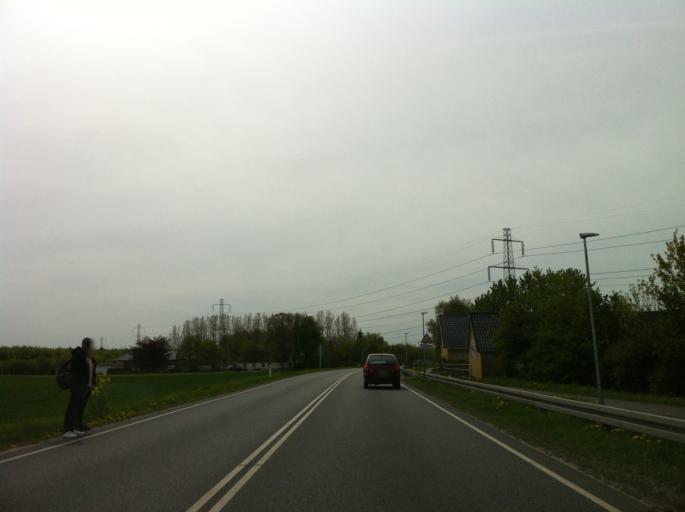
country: DK
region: Capital Region
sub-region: Egedal Kommune
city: Olstykke
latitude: 55.8171
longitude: 12.1657
